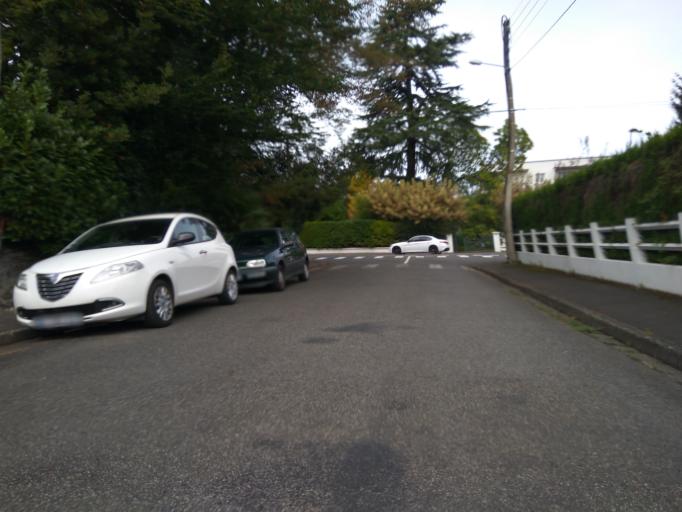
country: FR
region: Aquitaine
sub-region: Departement des Pyrenees-Atlantiques
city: Bizanos
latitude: 43.2984
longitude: -0.3446
